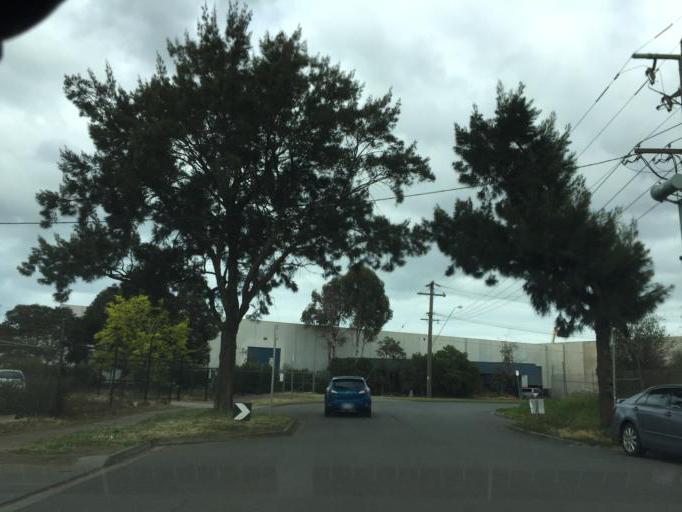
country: AU
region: Victoria
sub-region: Brimbank
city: Brooklyn
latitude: -37.8144
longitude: 144.8491
